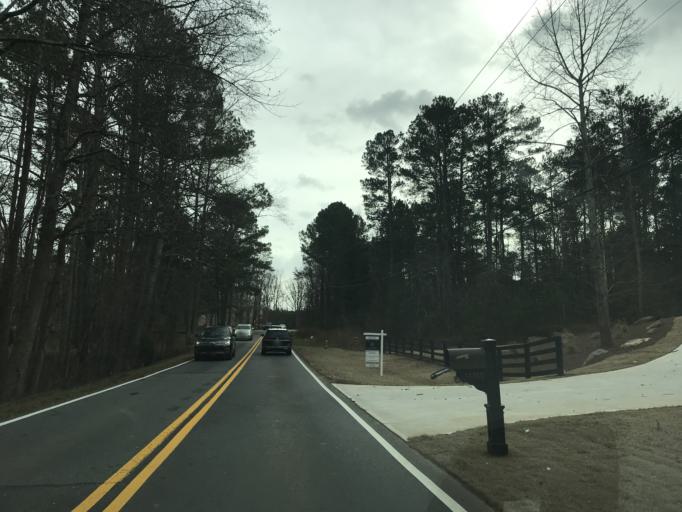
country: US
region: Georgia
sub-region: Fulton County
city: Milton
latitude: 34.1266
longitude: -84.2789
